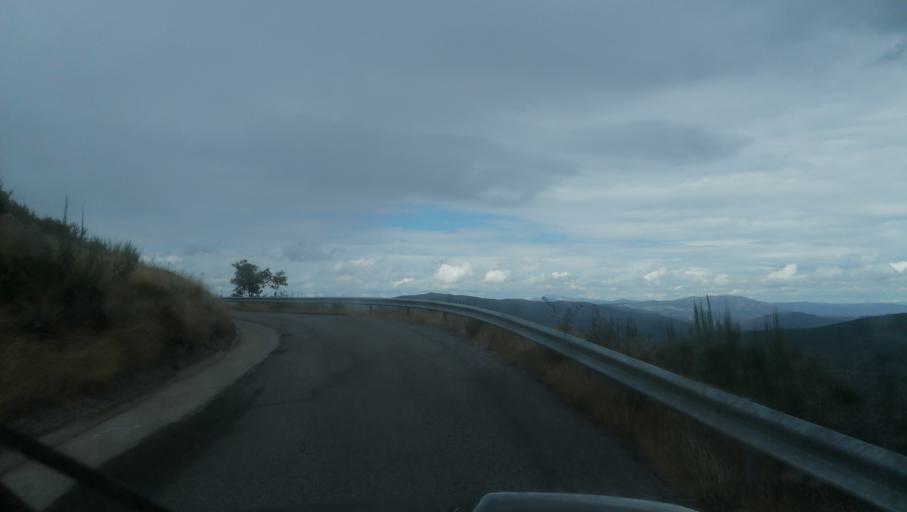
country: PT
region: Vila Real
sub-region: Vila Pouca de Aguiar
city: Vila Pouca de Aguiar
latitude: 41.5592
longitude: -7.6797
